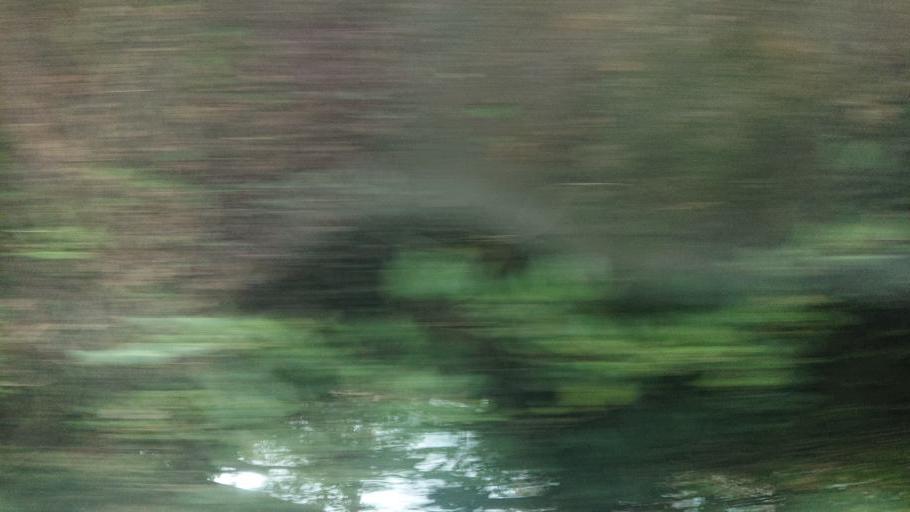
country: TW
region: Taiwan
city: Lugu
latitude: 23.6033
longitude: 120.7090
